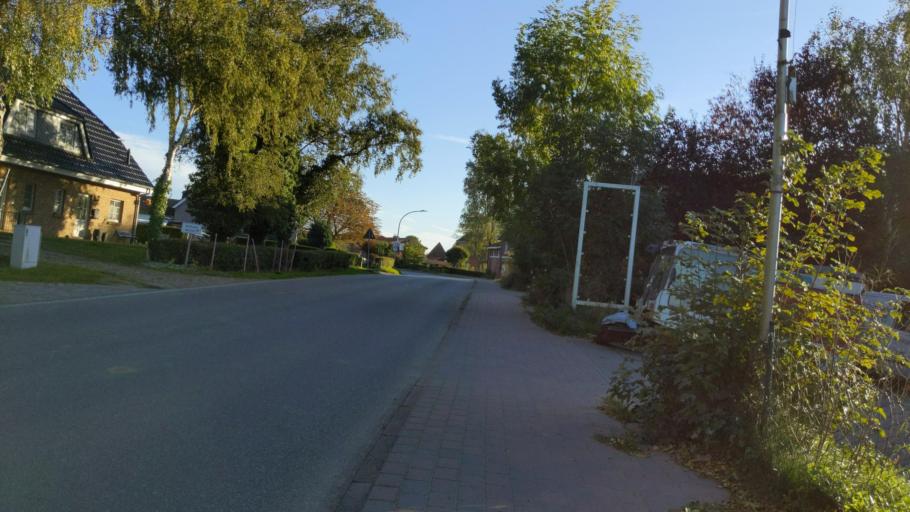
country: DE
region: Schleswig-Holstein
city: Ahrensbok
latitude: 54.0253
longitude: 10.5642
